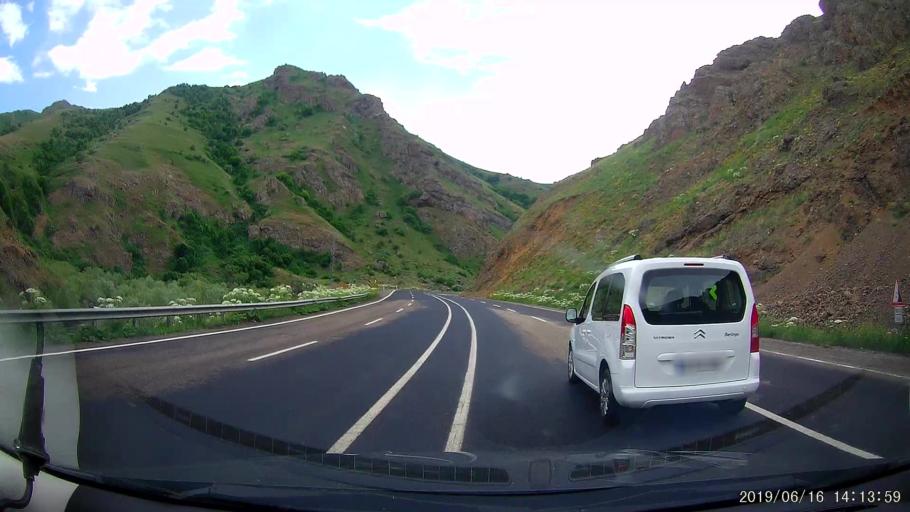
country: TR
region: Agri
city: Tahir
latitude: 39.7957
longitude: 42.5057
